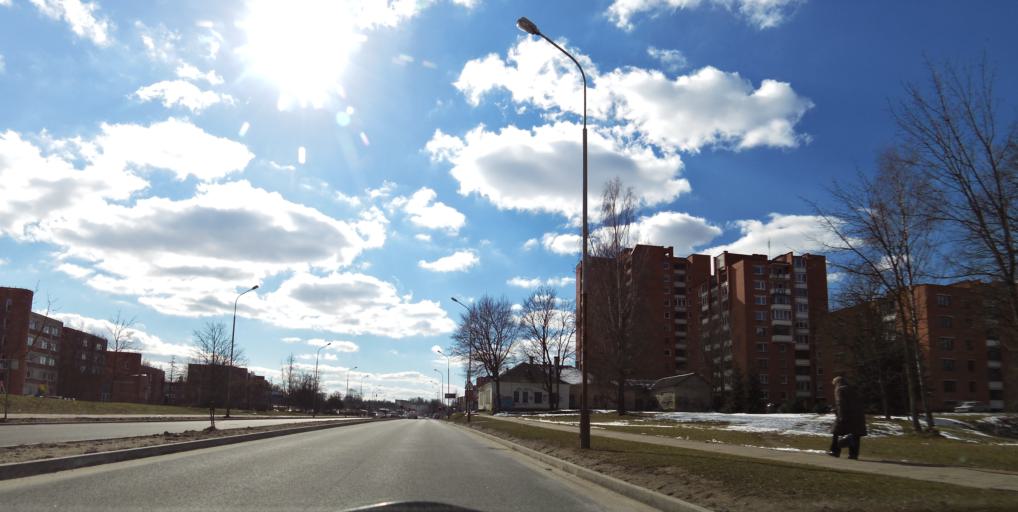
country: LT
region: Vilnius County
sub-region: Vilnius
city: Fabijoniskes
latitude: 54.7463
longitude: 25.2785
